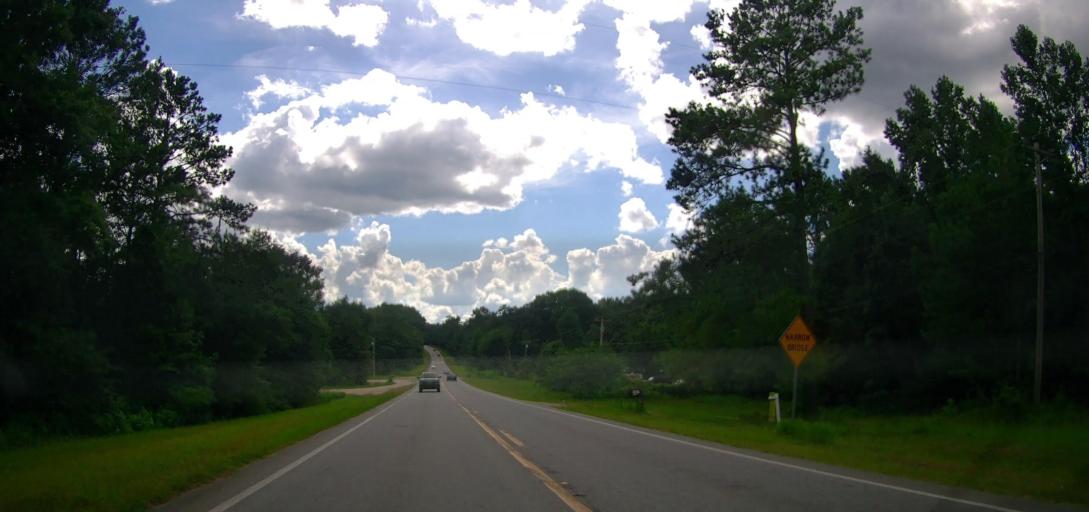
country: US
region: Alabama
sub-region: Russell County
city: Ladonia
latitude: 32.4440
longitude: -85.2841
